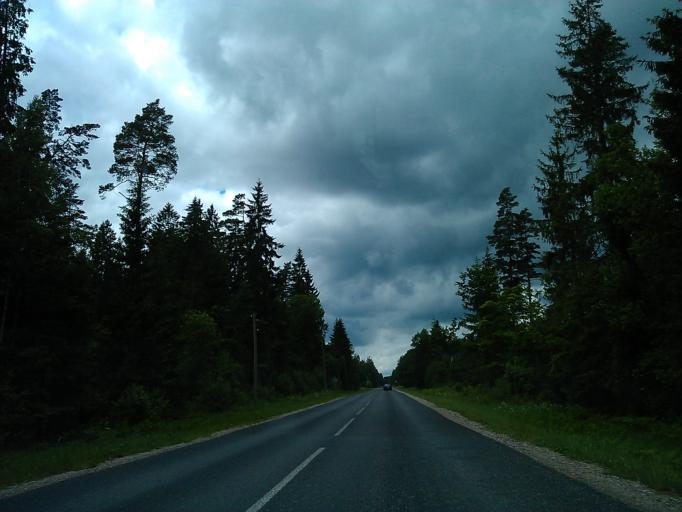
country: LV
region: Talsu Rajons
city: Stende
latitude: 57.0870
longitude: 22.4142
